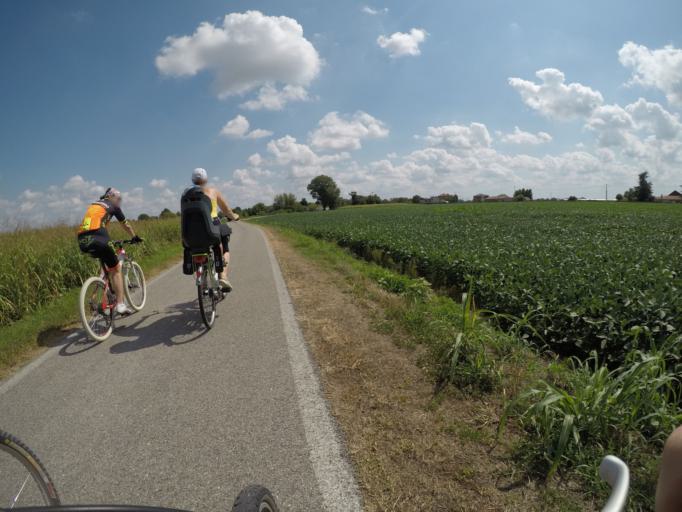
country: IT
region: Veneto
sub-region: Provincia di Rovigo
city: Lendinara
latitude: 45.0733
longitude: 11.6061
